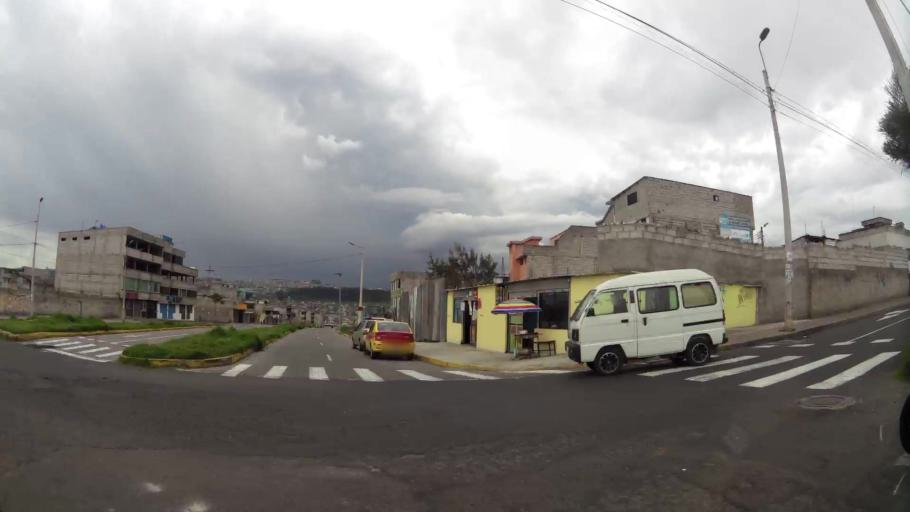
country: EC
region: Pichincha
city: Quito
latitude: -0.3144
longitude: -78.5534
